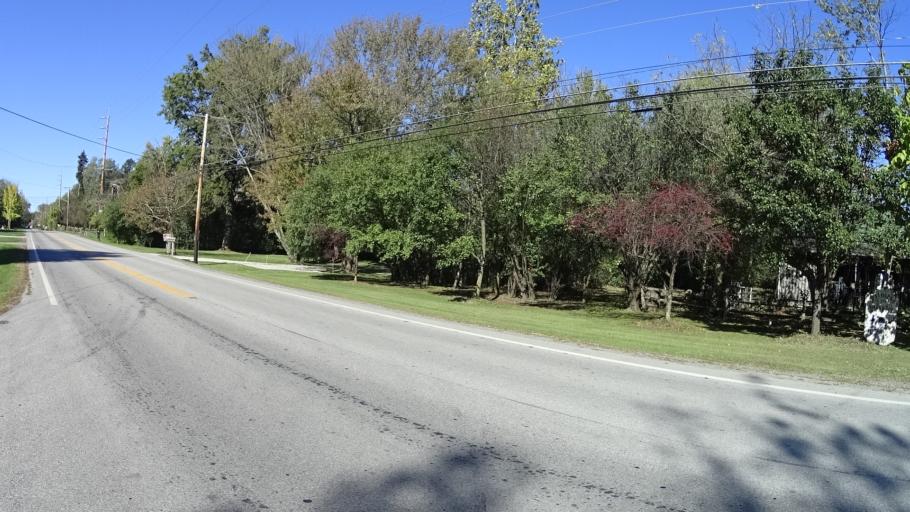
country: US
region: Ohio
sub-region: Lorain County
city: Oberlin
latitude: 41.2939
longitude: -82.1888
